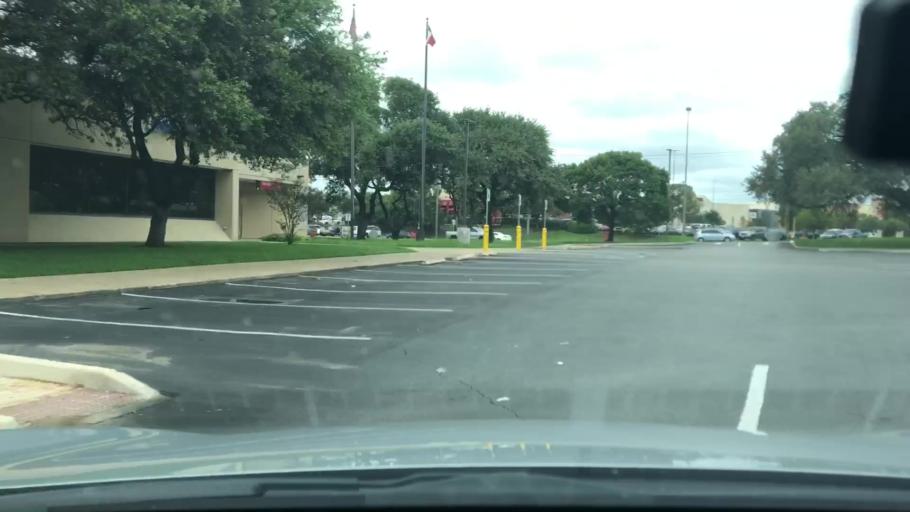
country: US
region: Texas
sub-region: Bexar County
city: Leon Valley
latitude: 29.4650
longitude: -98.6210
